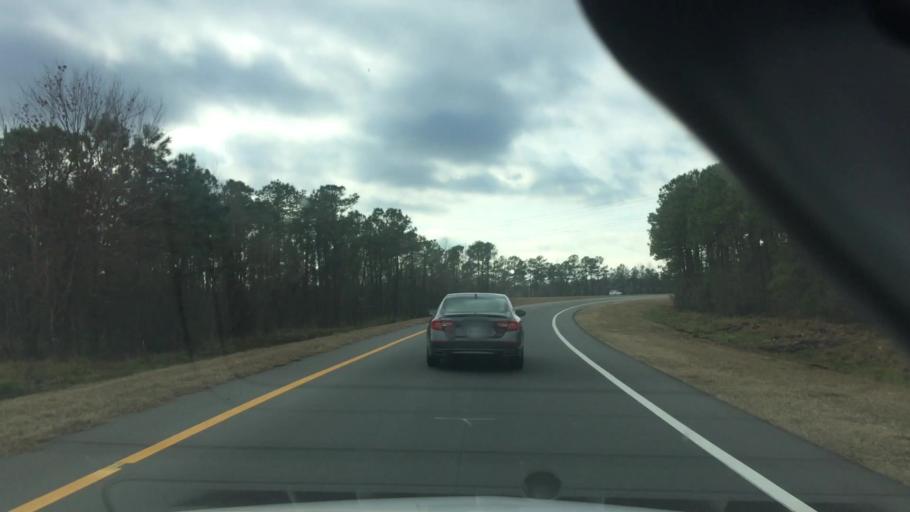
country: US
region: North Carolina
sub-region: New Hanover County
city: Murraysville
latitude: 34.3202
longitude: -77.8739
